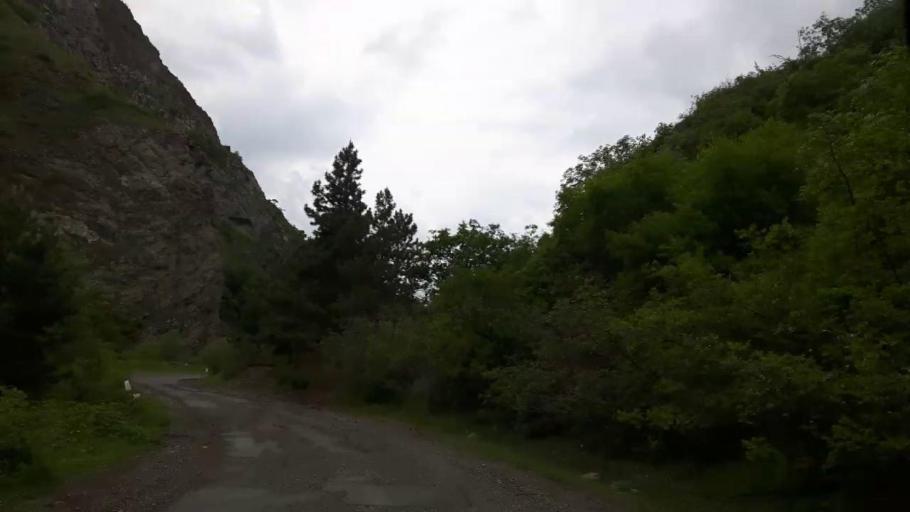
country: GE
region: Shida Kartli
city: Gori
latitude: 41.9011
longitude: 44.0642
